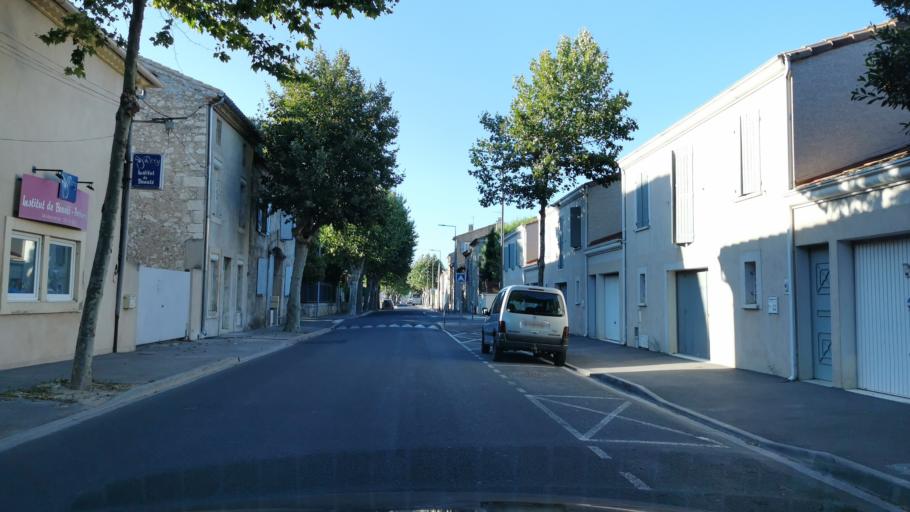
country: FR
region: Languedoc-Roussillon
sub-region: Departement de l'Aude
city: Moussan
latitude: 43.2453
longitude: 2.9974
